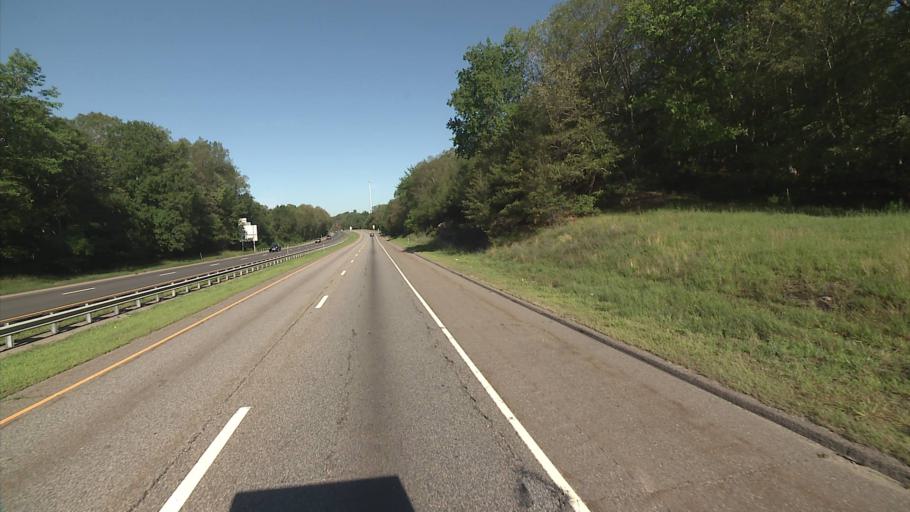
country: US
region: Connecticut
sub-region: New London County
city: Lisbon
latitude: 41.5900
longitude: -72.0088
